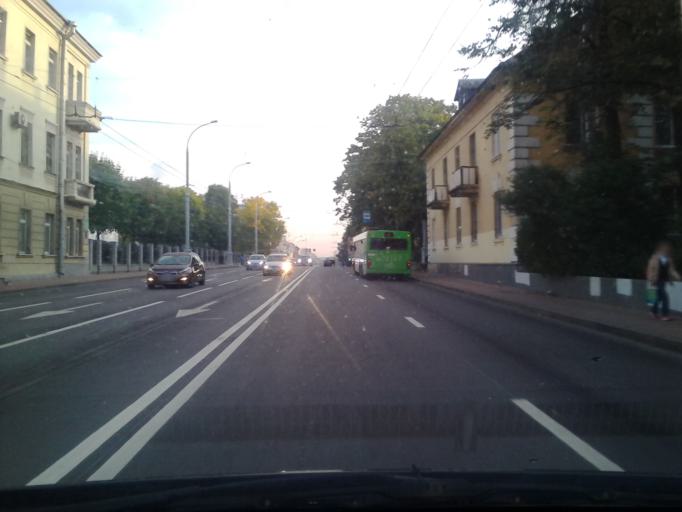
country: BY
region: Minsk
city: Minsk
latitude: 53.9135
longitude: 27.5613
